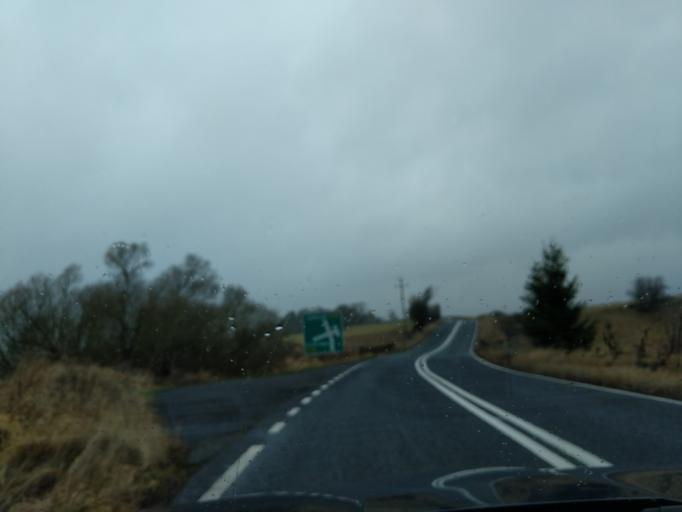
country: GB
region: England
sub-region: Northumberland
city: Rochester
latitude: 55.2474
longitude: -2.2180
